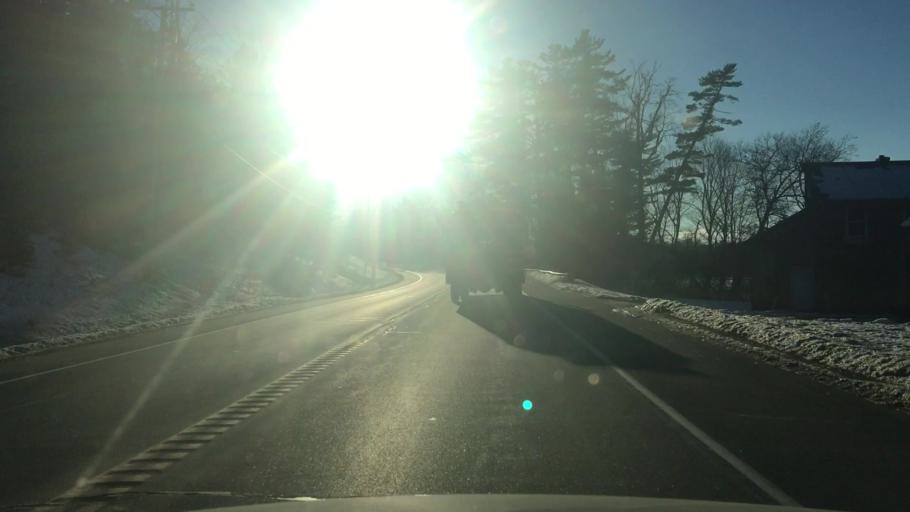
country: US
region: Maine
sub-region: Somerset County
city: Norridgewock
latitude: 44.7202
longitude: -69.7844
